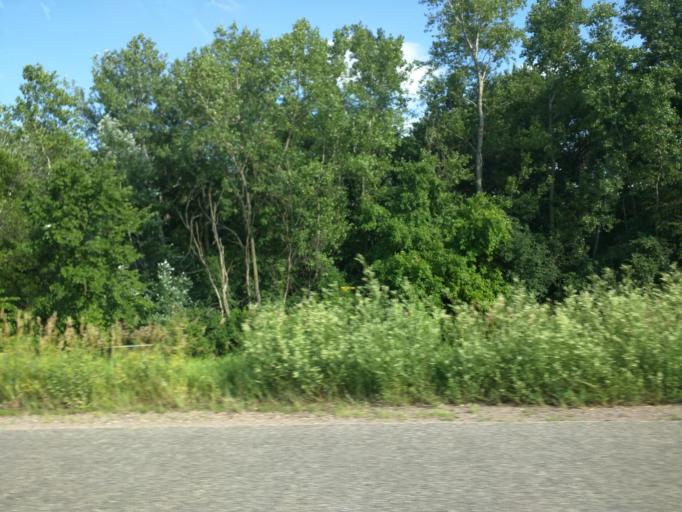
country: US
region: Minnesota
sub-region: Hennepin County
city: Minnetonka Mills
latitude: 44.9291
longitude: -93.4316
